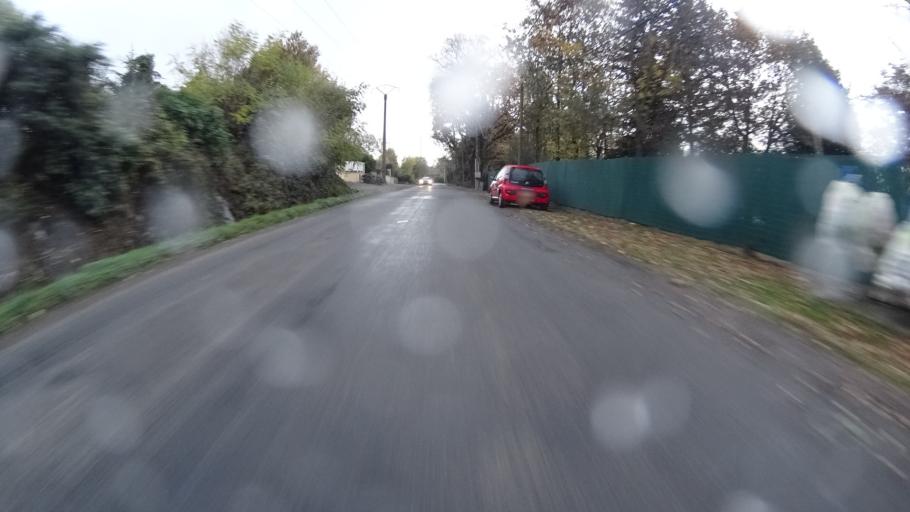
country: FR
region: Pays de la Loire
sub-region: Departement de la Loire-Atlantique
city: Saint-Nicolas-de-Redon
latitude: 47.6755
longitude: -2.0428
